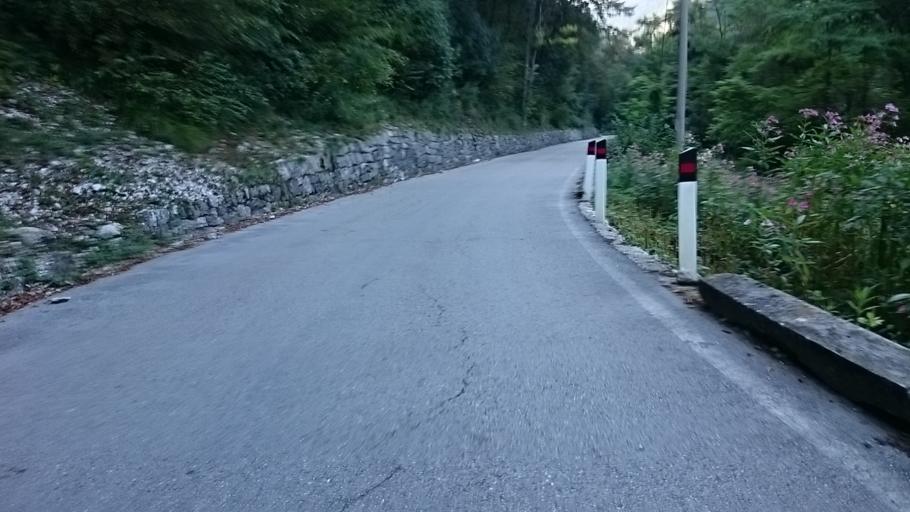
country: IT
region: Veneto
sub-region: Provincia di Vicenza
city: Cismon del Grappa
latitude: 45.9310
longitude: 11.7239
